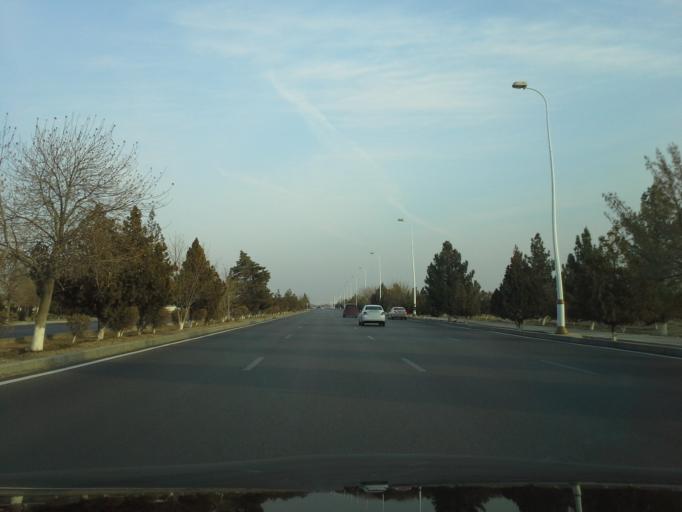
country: TM
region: Ahal
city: Abadan
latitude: 38.0381
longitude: 58.2158
